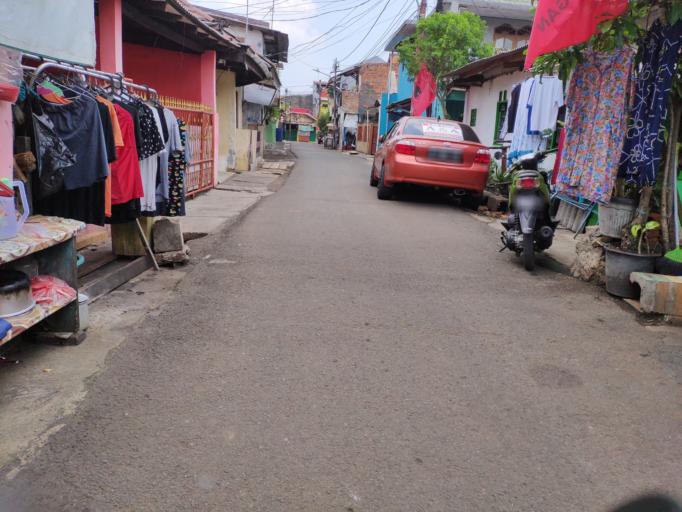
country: ID
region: Jakarta Raya
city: Jakarta
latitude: -6.2111
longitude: 106.8638
